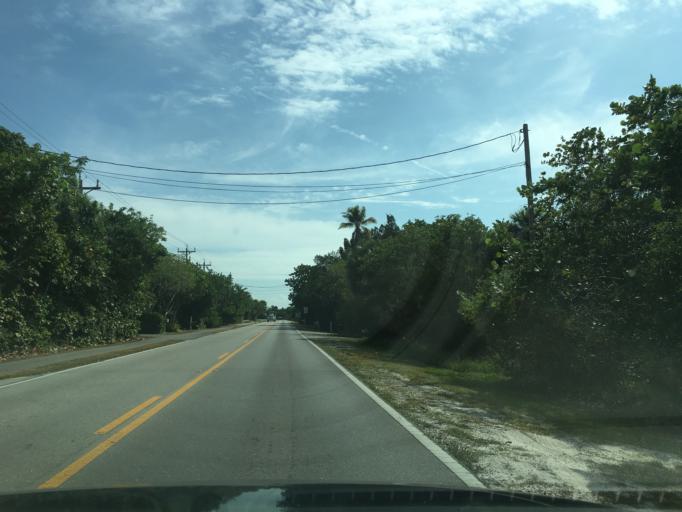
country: US
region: Florida
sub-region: Lee County
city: Saint James City
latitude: 26.4726
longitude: -82.1662
